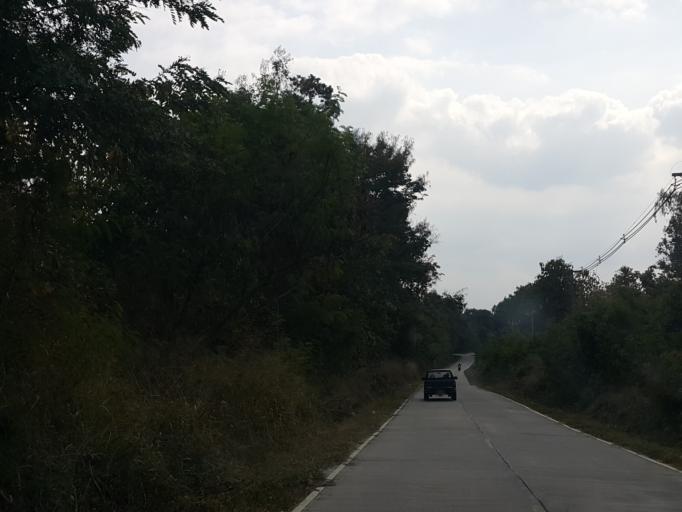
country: TH
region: Chiang Mai
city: Mae On
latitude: 18.8263
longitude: 99.2137
